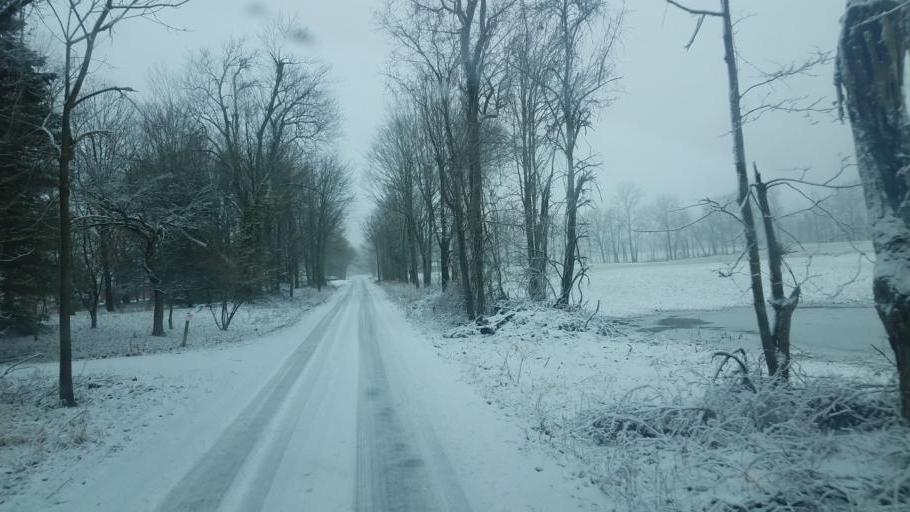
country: US
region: Ohio
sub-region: Richland County
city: Ontario
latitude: 40.7591
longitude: -82.6634
